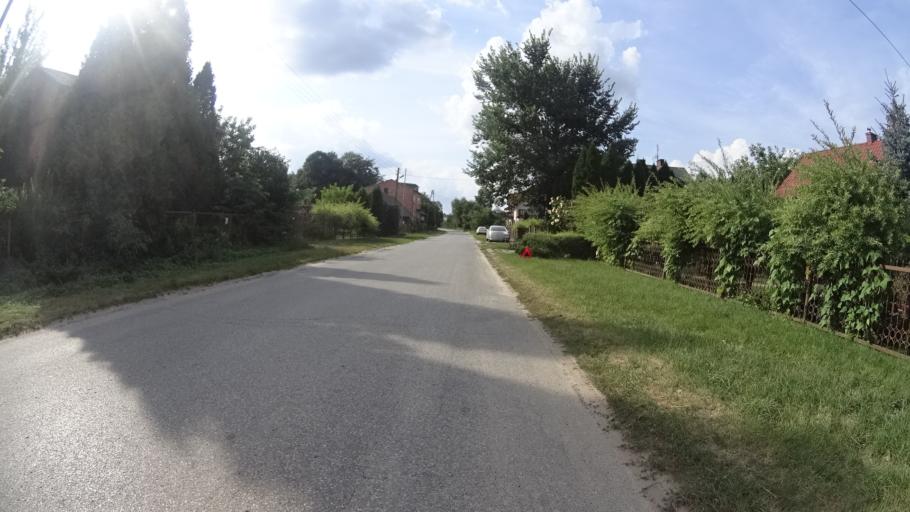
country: PL
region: Masovian Voivodeship
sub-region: Powiat bialobrzeski
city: Wysmierzyce
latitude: 51.6536
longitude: 20.7671
